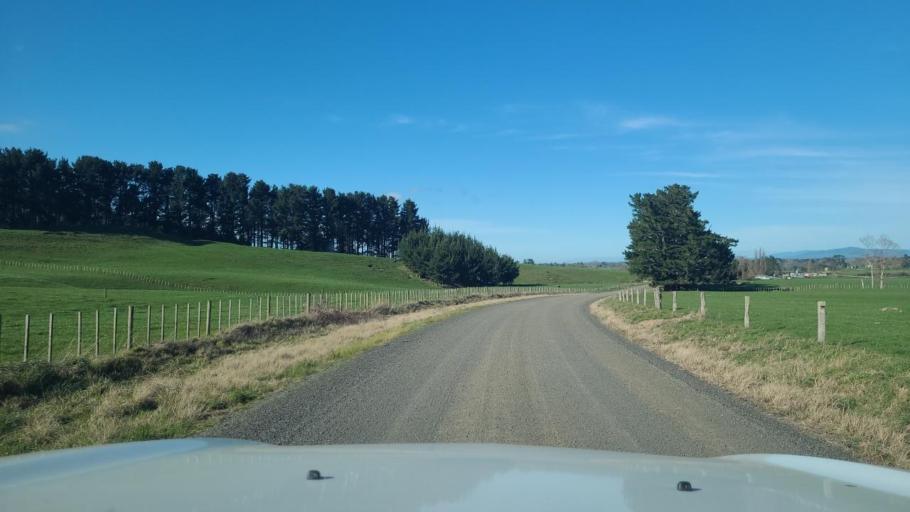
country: NZ
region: Bay of Plenty
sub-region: Western Bay of Plenty District
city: Katikati
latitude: -37.6072
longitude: 175.7972
